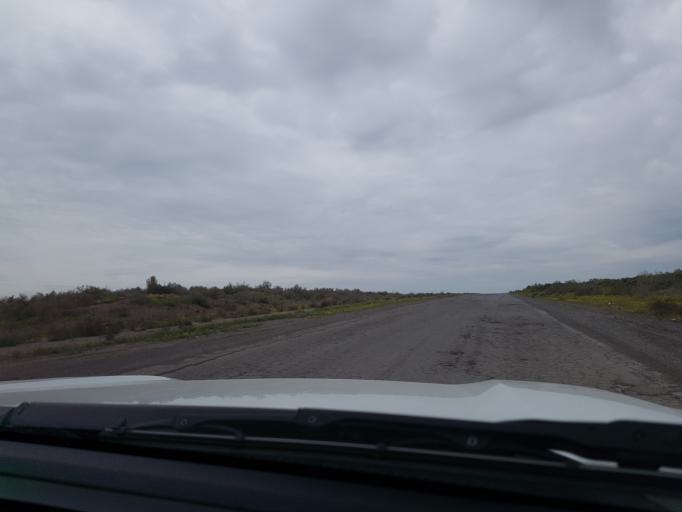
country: TM
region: Mary
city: Bayramaly
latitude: 37.9137
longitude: 62.6216
